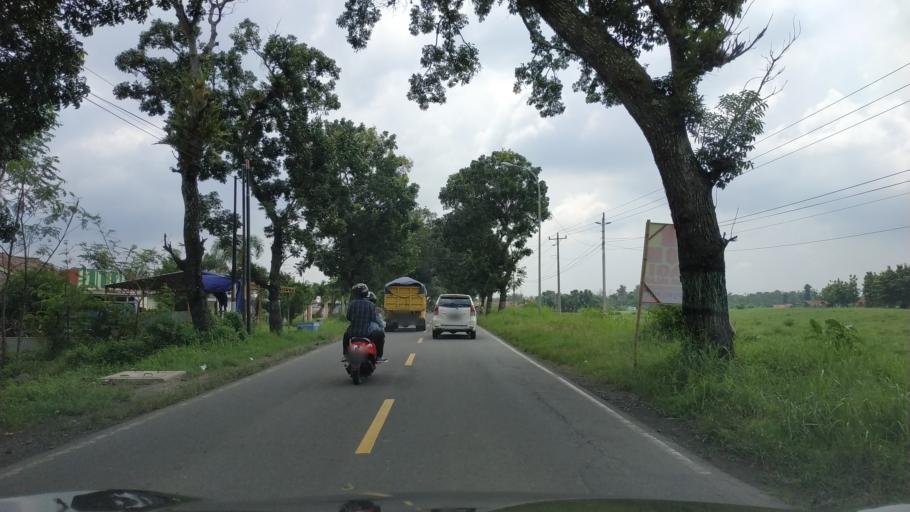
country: ID
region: Central Java
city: Lebaksiu
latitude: -7.0273
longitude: 109.1431
